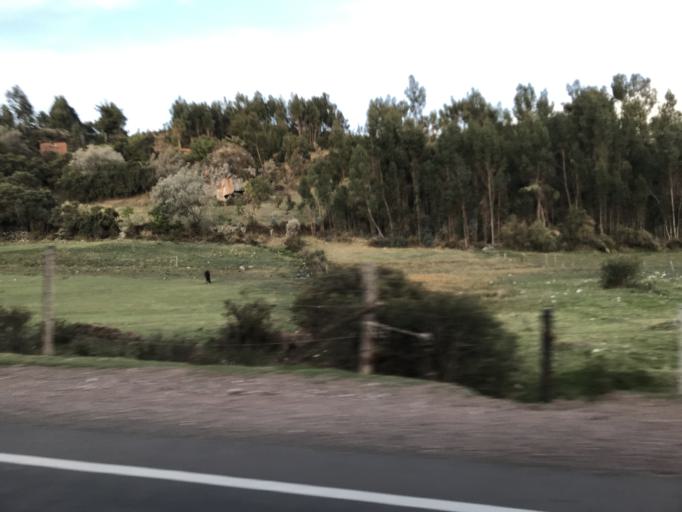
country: PE
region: Cusco
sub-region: Provincia de Cusco
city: Cusco
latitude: -13.4957
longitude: -71.9730
